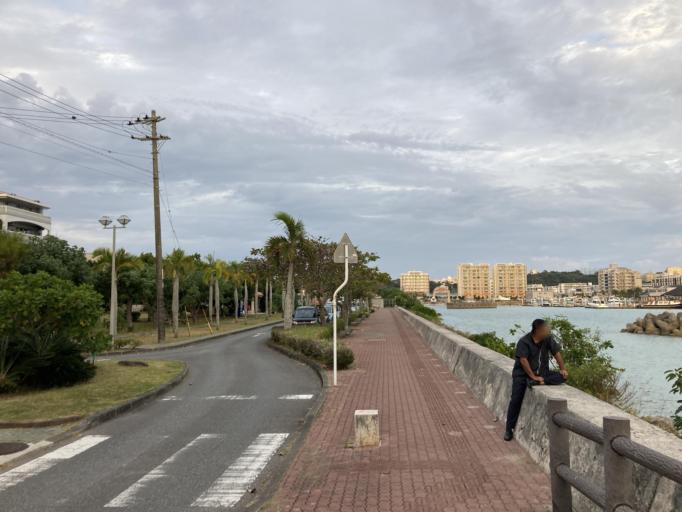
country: JP
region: Okinawa
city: Chatan
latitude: 26.3213
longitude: 127.7513
